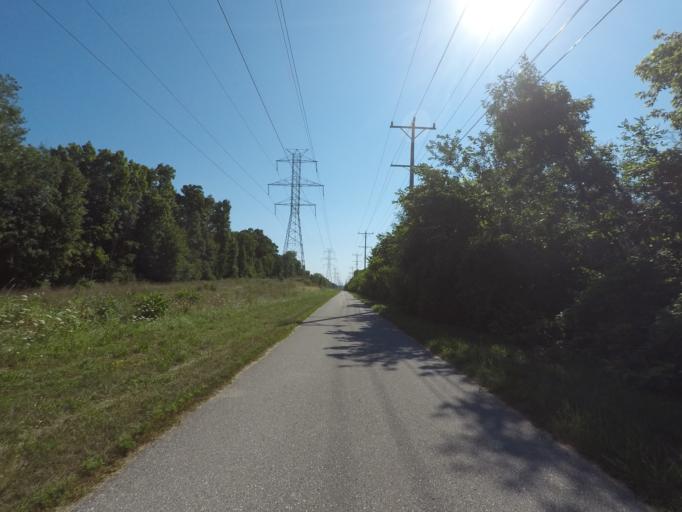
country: US
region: Wisconsin
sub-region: Waukesha County
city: Elm Grove
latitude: 43.0102
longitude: -88.0766
